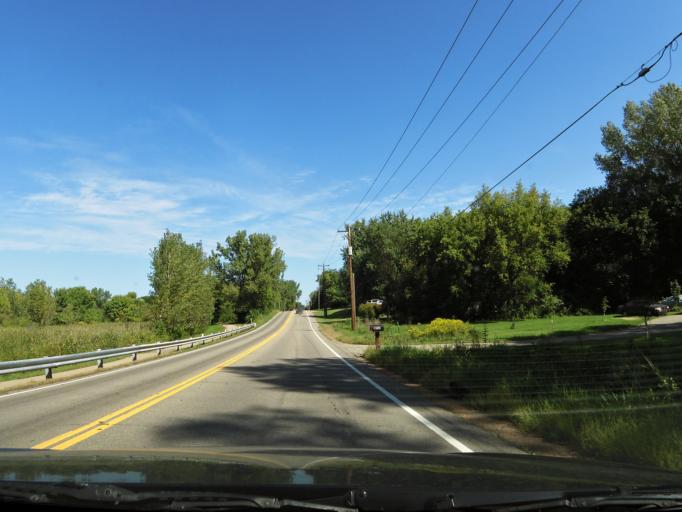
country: US
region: Minnesota
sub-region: Carver County
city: Chanhassen
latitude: 44.8812
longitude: -93.5208
